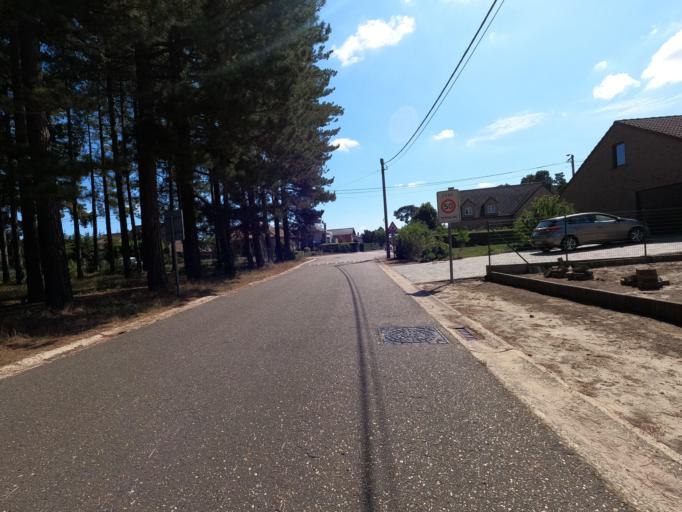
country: BE
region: Flanders
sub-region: Provincie Vlaams-Brabant
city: Scherpenheuvel-Zichem
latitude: 51.0241
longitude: 4.9910
